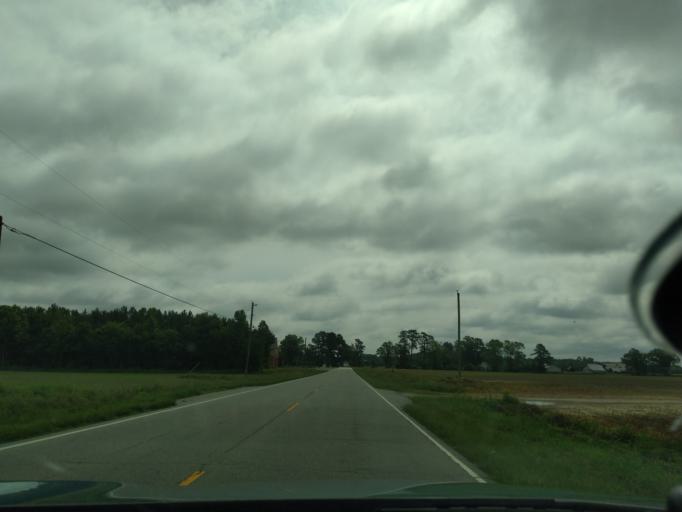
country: US
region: North Carolina
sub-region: Washington County
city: Plymouth
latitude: 35.8761
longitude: -76.6450
